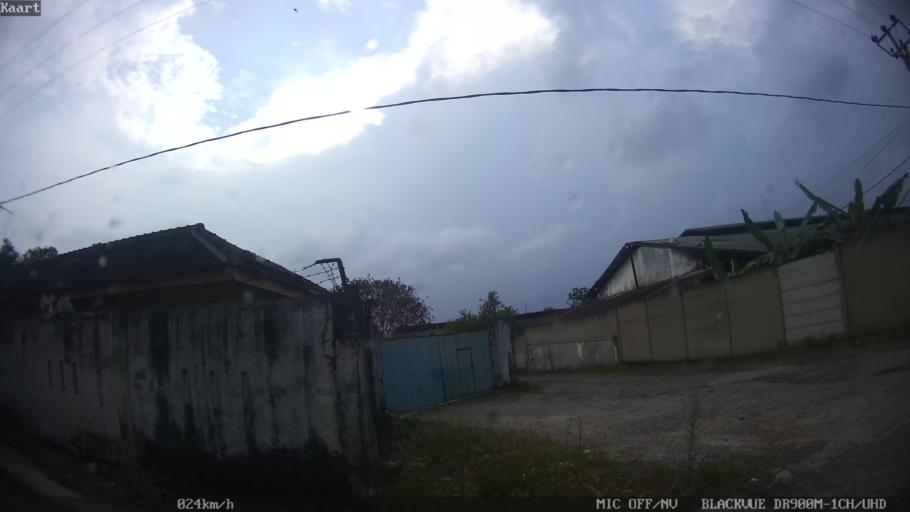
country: ID
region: Lampung
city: Bandarlampung
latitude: -5.4139
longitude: 105.2938
